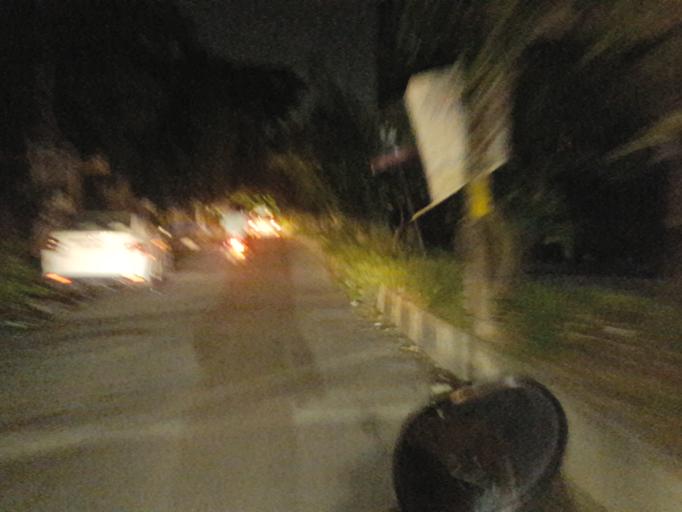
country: IN
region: Telangana
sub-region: Rangareddi
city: Kukatpalli
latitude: 17.4814
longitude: 78.3918
